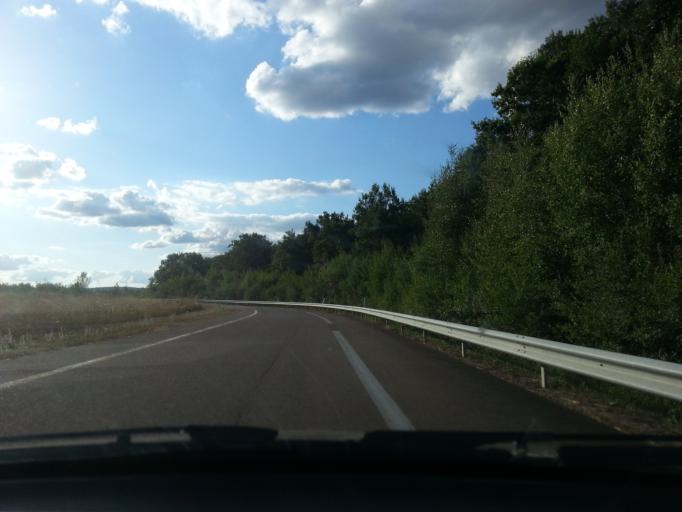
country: FR
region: Bourgogne
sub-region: Departement de Saone-et-Loire
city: Dracy-le-Fort
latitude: 46.7579
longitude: 4.7794
